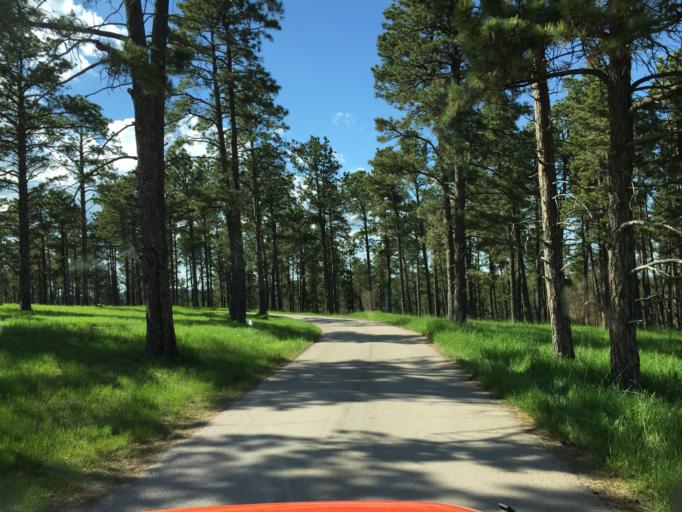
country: US
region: South Dakota
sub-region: Pennington County
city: Colonial Pine Hills
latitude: 43.9781
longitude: -103.3003
